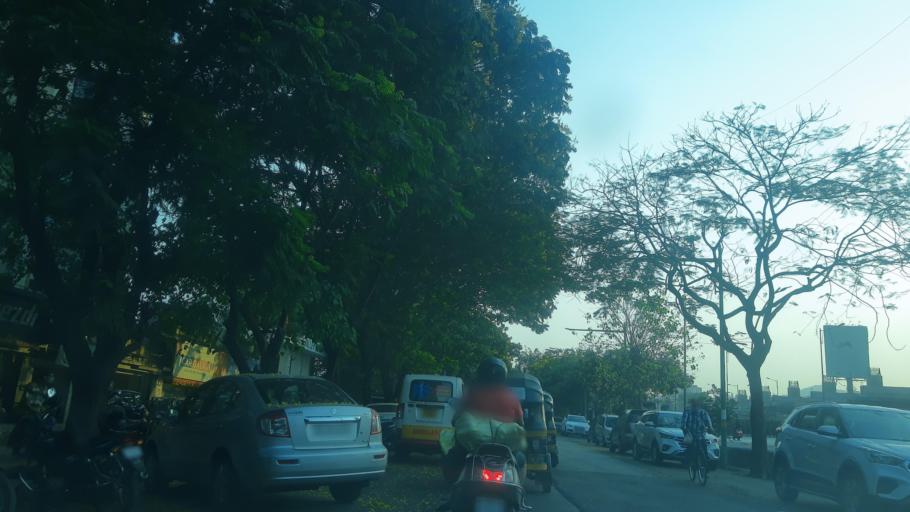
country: IN
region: Maharashtra
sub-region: Thane
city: Thane
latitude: 19.2070
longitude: 72.9719
